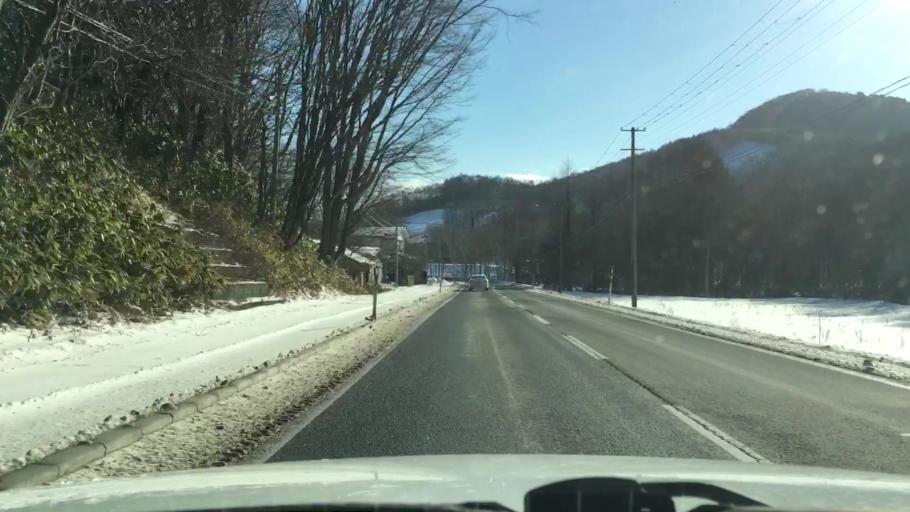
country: JP
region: Iwate
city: Morioka-shi
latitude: 39.6433
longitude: 141.3755
